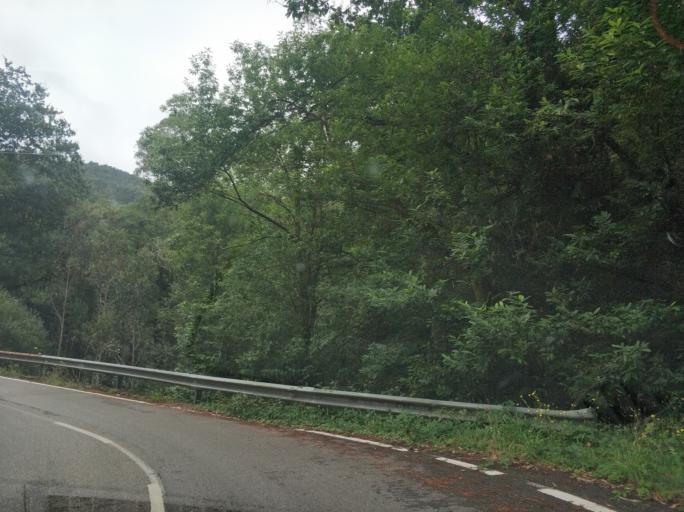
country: ES
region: Asturias
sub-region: Province of Asturias
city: Salas
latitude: 43.5566
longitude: -6.2951
